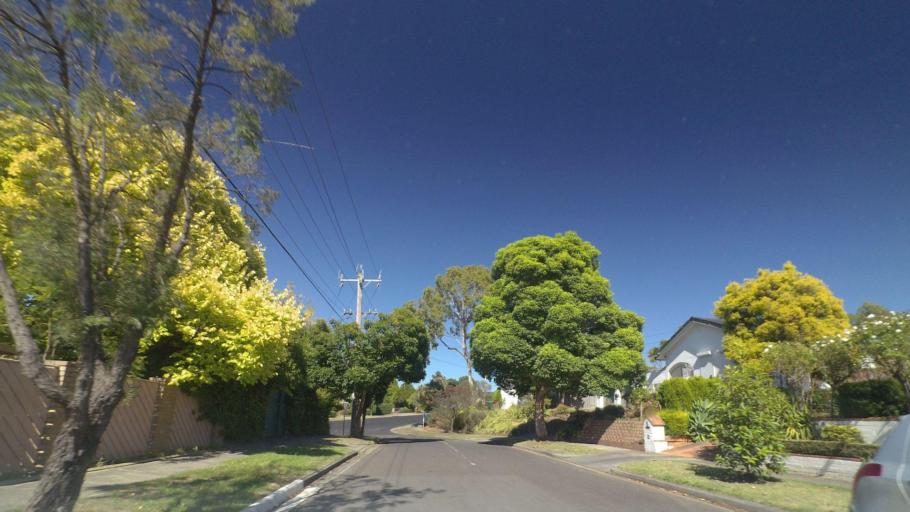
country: AU
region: Victoria
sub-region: Manningham
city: Donvale
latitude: -37.7827
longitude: 145.1721
